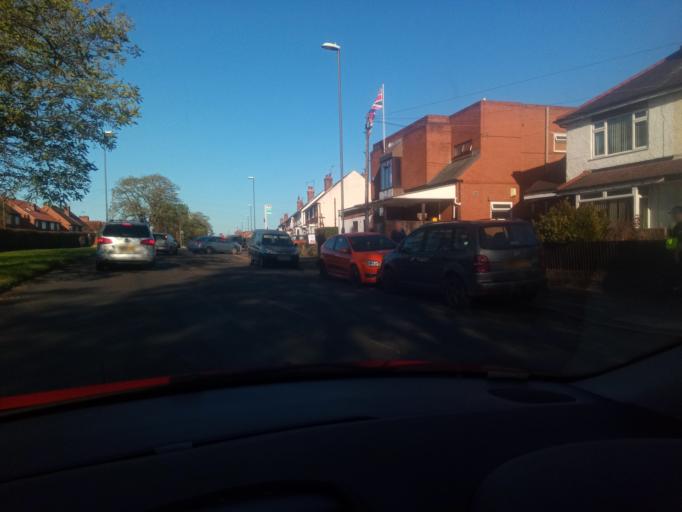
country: GB
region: England
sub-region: Derby
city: Derby
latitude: 52.8859
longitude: -1.4497
